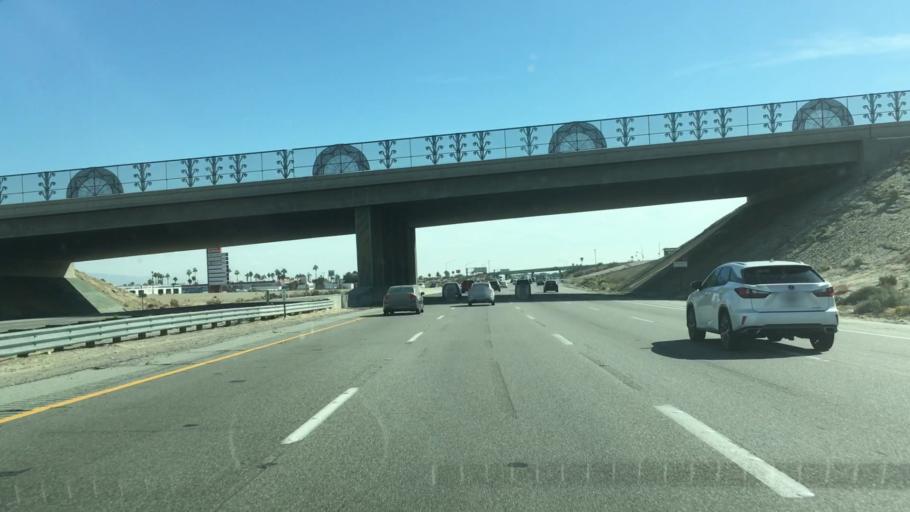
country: US
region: California
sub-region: Riverside County
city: Thousand Palms
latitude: 33.8204
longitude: -116.4096
